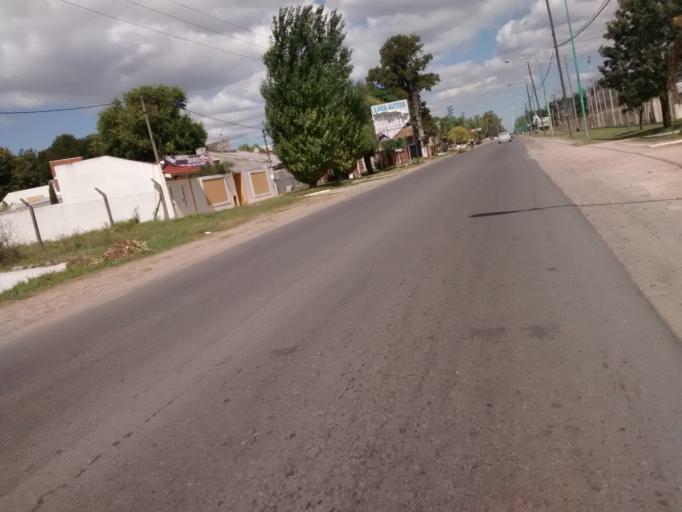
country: AR
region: Buenos Aires
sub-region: Partido de La Plata
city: La Plata
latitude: -34.9613
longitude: -57.9568
